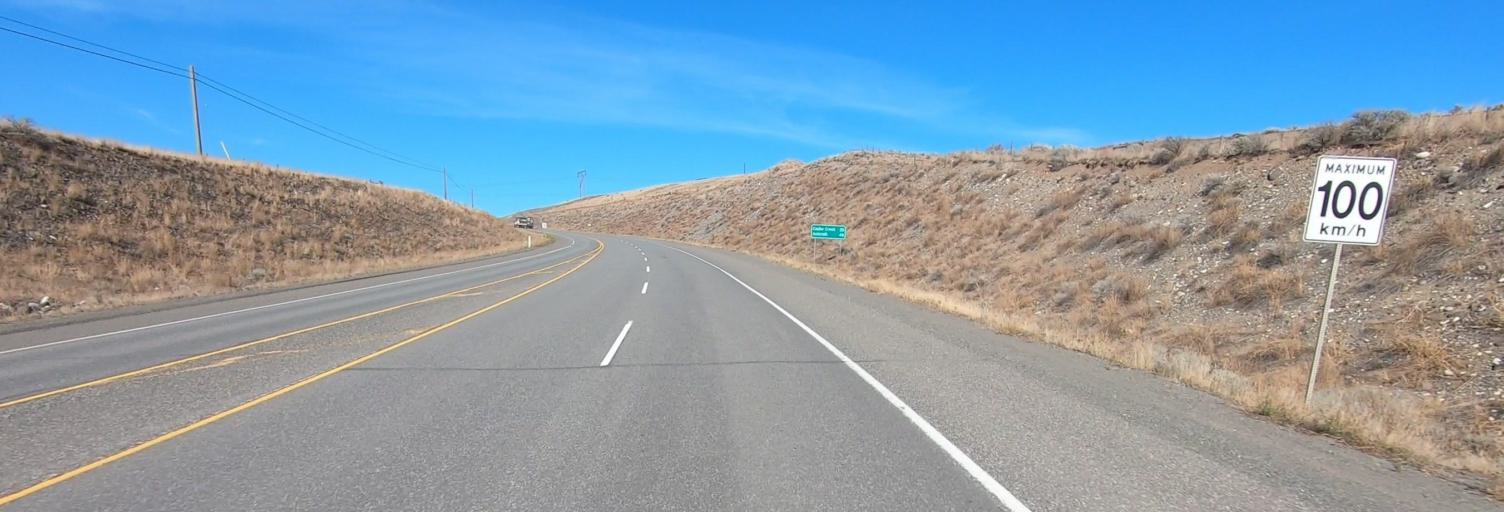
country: CA
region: British Columbia
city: Logan Lake
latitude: 50.7582
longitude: -120.8780
